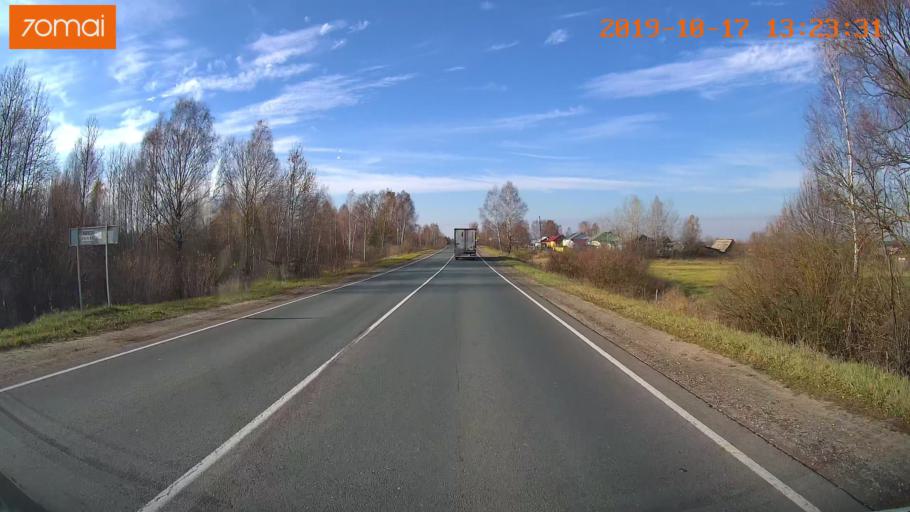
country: RU
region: Rjazan
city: Gus'-Zheleznyy
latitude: 55.0898
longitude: 40.9784
